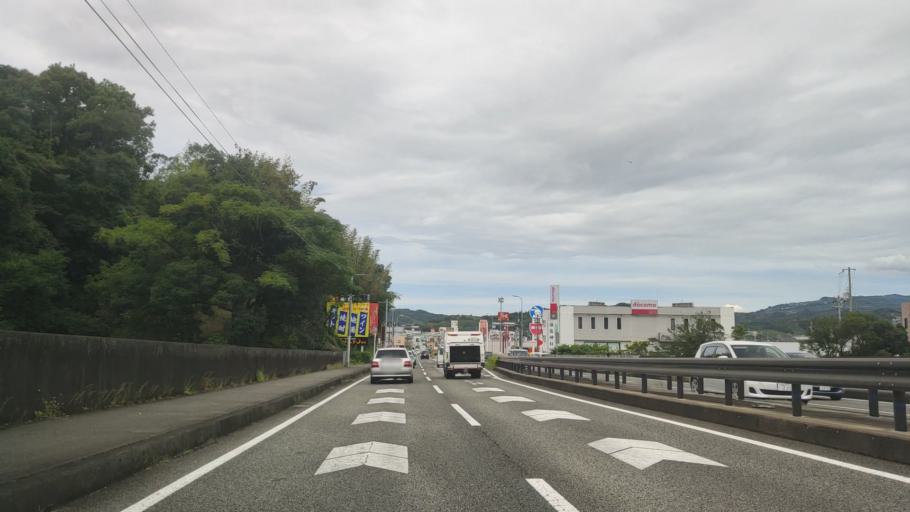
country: JP
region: Wakayama
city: Tanabe
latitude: 33.7370
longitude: 135.3974
